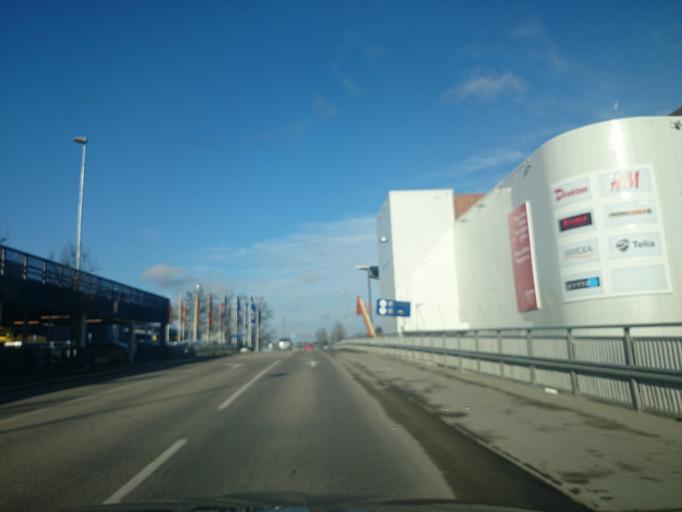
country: SE
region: Stockholm
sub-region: Huddinge Kommun
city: Segeltorp
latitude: 59.2696
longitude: 17.9150
